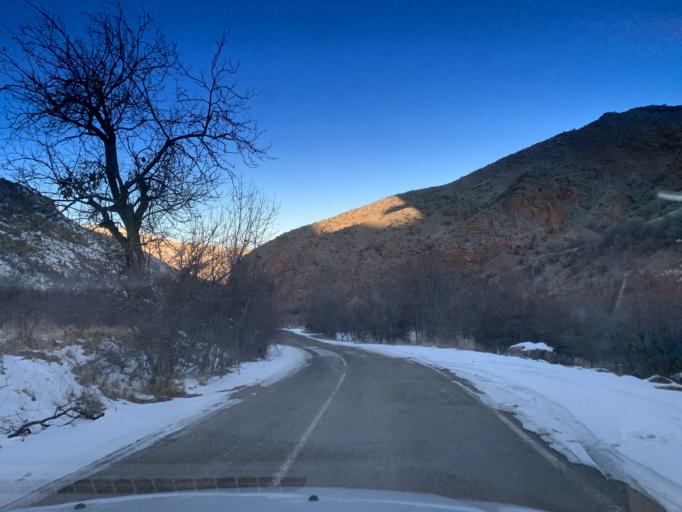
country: AM
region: Vayots' Dzori Marz
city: Areni
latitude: 39.6848
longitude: 45.2279
